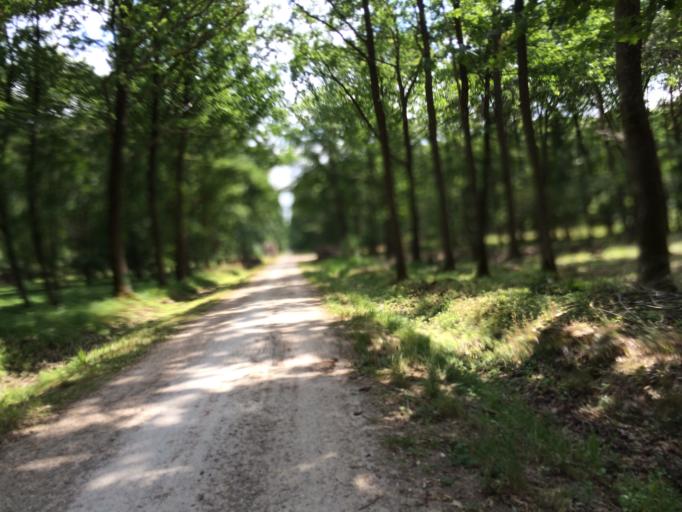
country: FR
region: Ile-de-France
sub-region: Departement de l'Essonne
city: Epinay-sous-Senart
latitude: 48.6672
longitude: 2.5013
